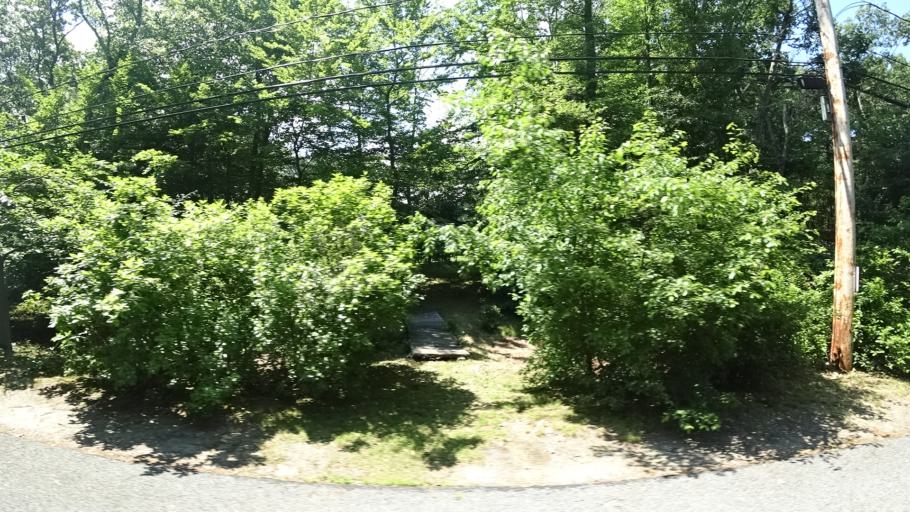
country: US
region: Massachusetts
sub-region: Norfolk County
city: Dedham
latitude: 42.2408
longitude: -71.1892
